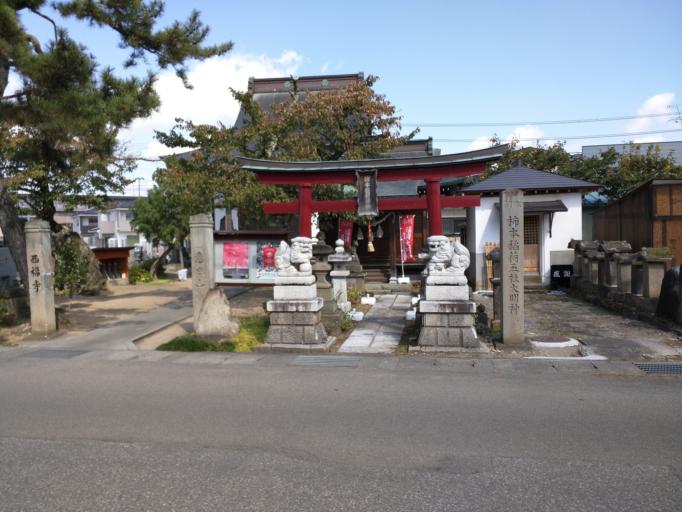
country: JP
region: Fukushima
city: Kitakata
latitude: 37.5020
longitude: 139.9152
